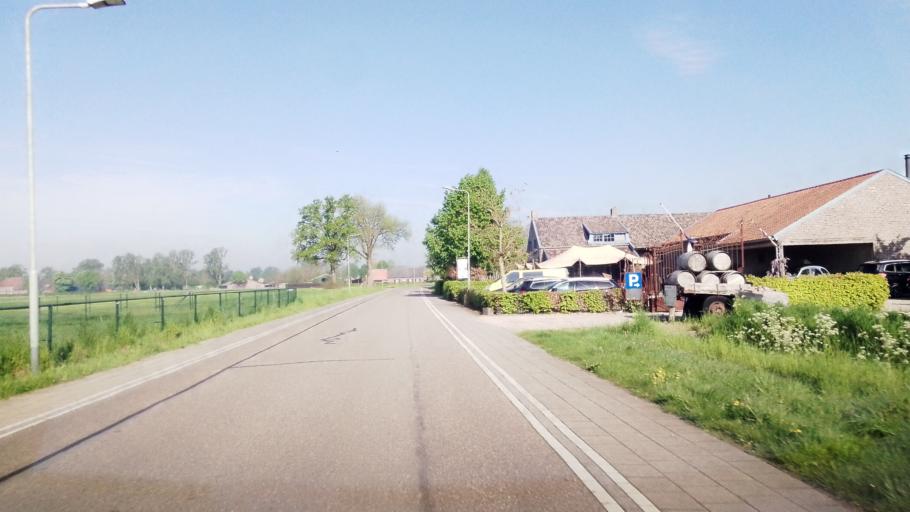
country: NL
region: Limburg
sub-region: Gemeente Peel en Maas
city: Maasbree
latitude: 51.4132
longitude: 6.0194
